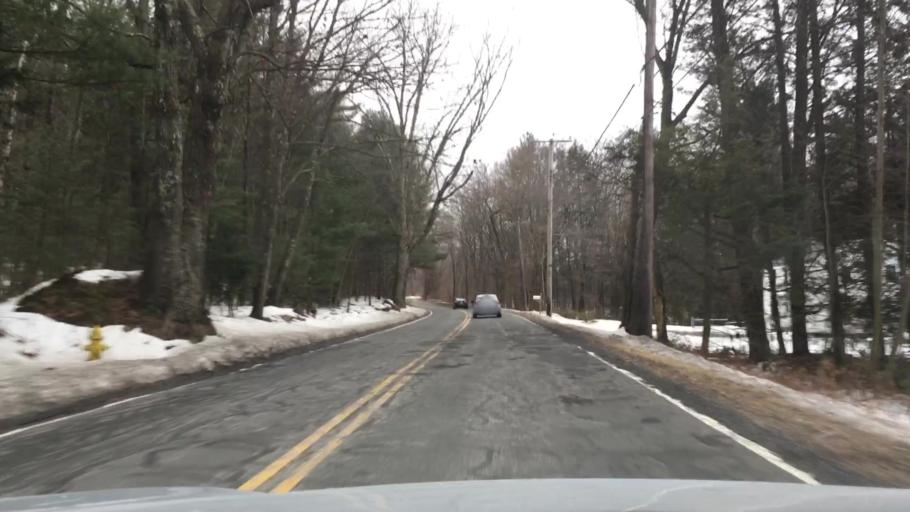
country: US
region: Massachusetts
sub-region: Hampden County
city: Southwick
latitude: 42.0740
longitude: -72.7233
